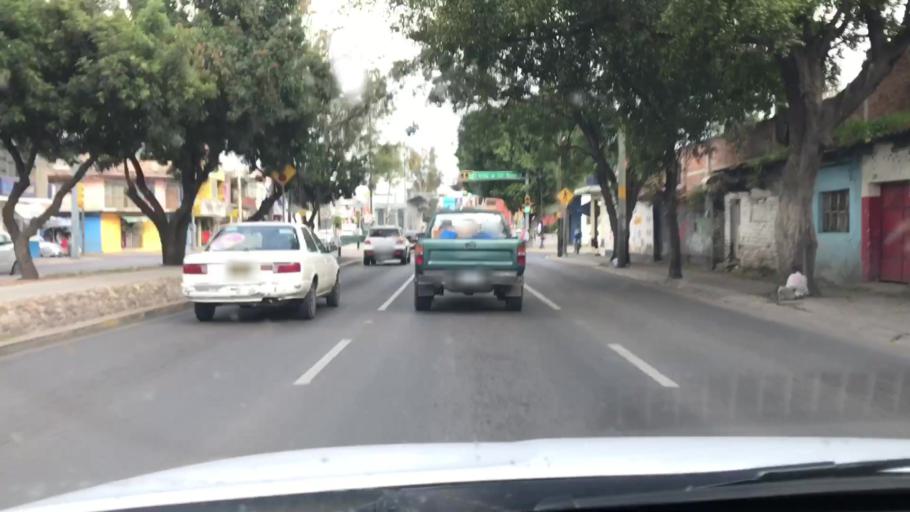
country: MX
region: Guanajuato
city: Leon
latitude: 21.1023
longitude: -101.6862
